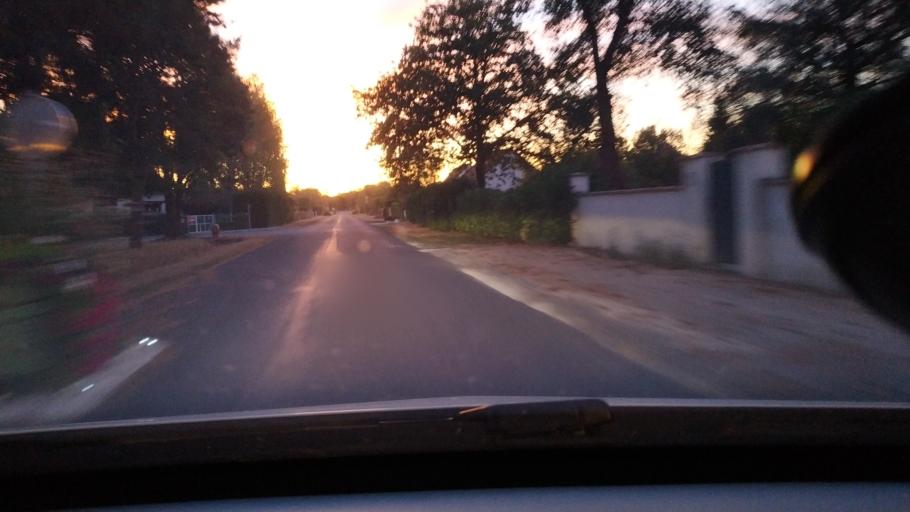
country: FR
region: Centre
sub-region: Departement du Cher
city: Brinon-sur-Sauldre
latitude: 47.6094
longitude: 2.1701
